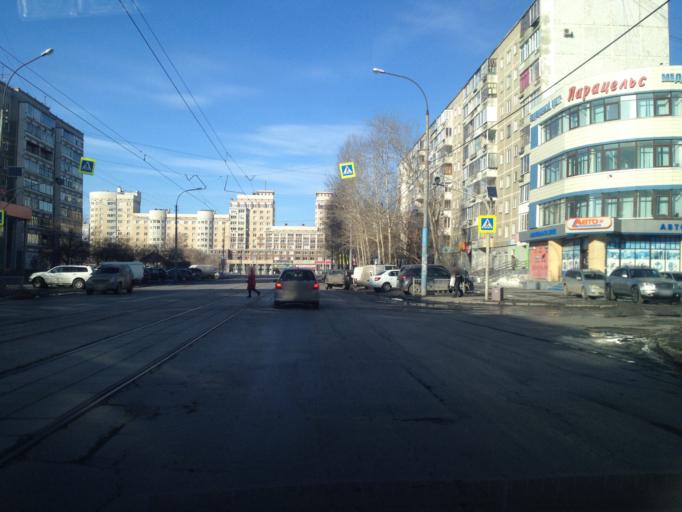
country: RU
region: Sverdlovsk
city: Yekaterinburg
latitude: 56.8335
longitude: 60.5454
